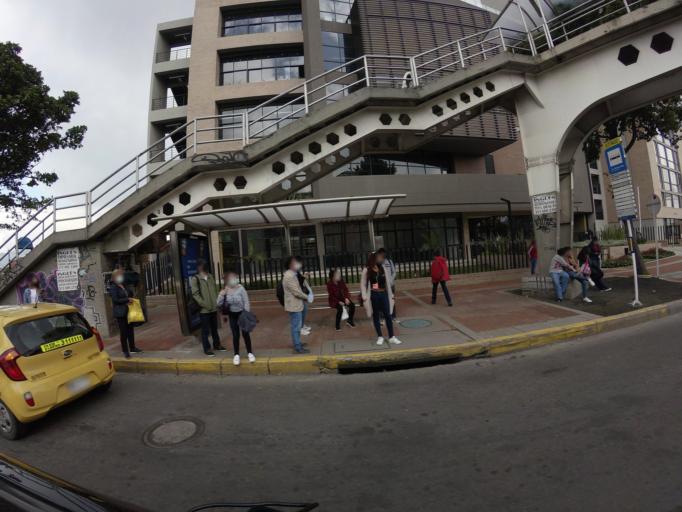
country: CO
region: Bogota D.C.
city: Barrio San Luis
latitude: 4.7105
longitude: -74.0711
